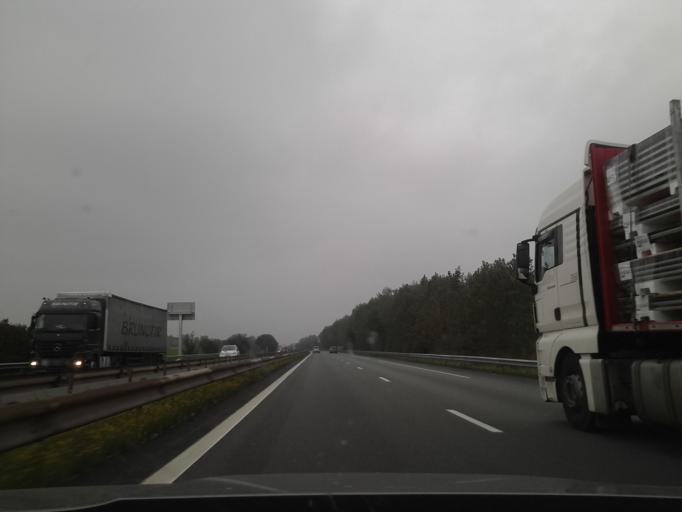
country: FR
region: Nord-Pas-de-Calais
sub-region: Departement du Nord
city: Lieu-Saint-Amand
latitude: 50.2820
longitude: 3.3464
